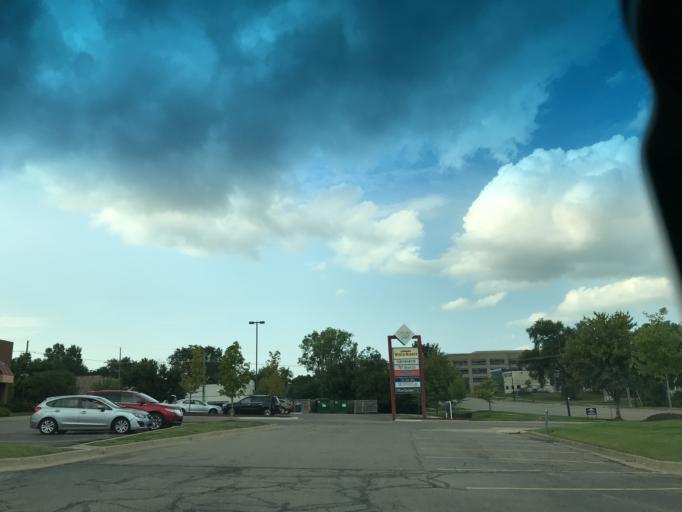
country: US
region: Michigan
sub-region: Washtenaw County
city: Ann Arbor
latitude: 42.2449
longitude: -83.7398
